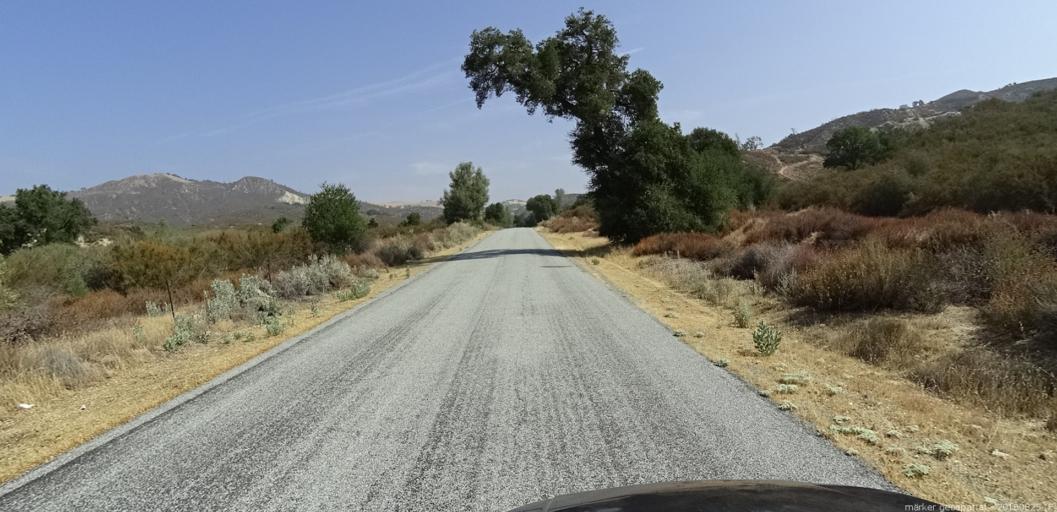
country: US
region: California
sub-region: San Luis Obispo County
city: San Miguel
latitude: 35.8957
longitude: -120.5544
